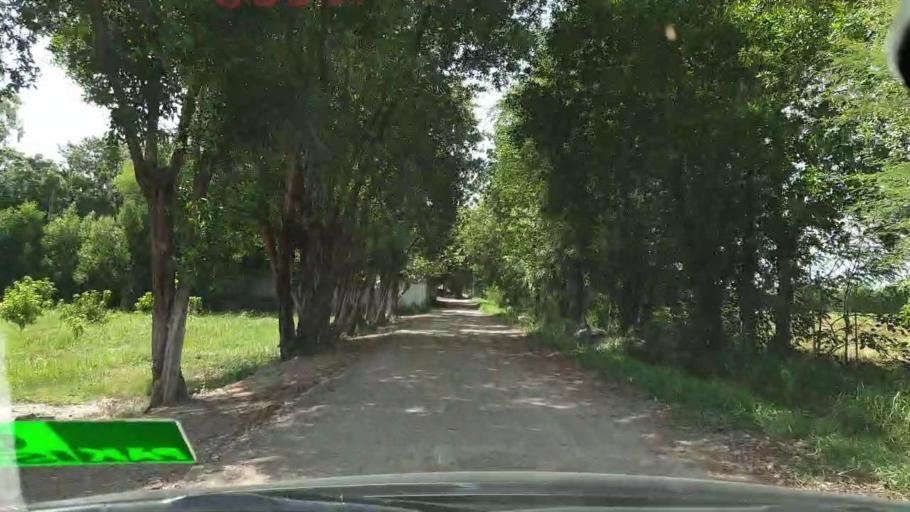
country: PK
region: Sindh
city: Kadhan
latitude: 24.6175
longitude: 69.1834
